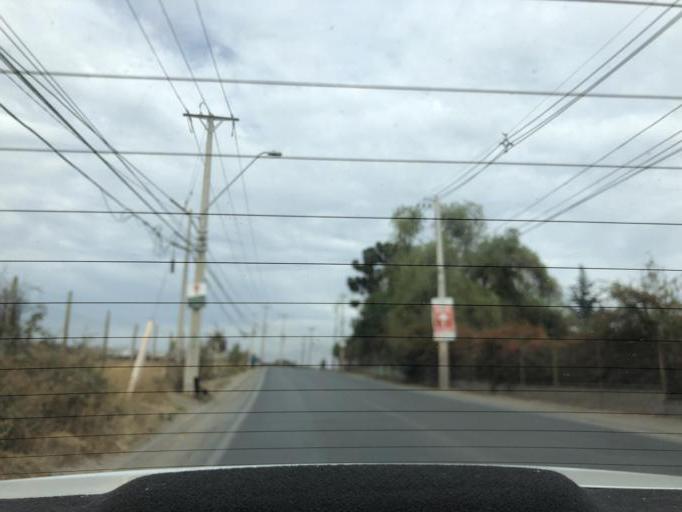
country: CL
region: Santiago Metropolitan
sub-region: Provincia de Cordillera
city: Puente Alto
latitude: -33.6055
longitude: -70.5341
